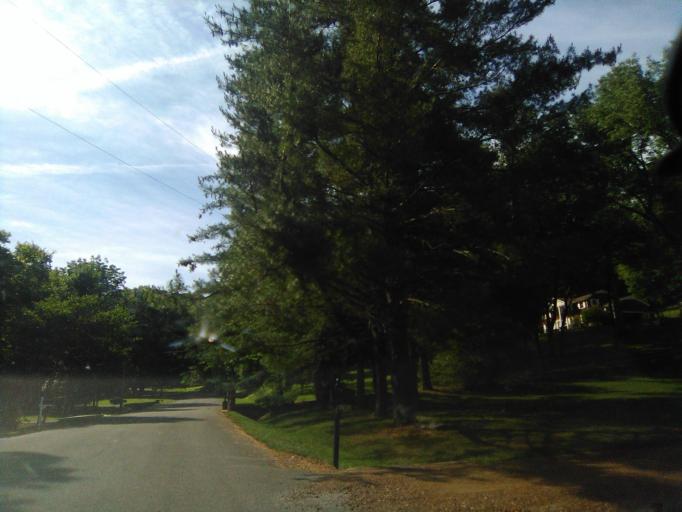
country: US
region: Tennessee
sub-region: Davidson County
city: Belle Meade
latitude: 36.1125
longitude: -86.9069
